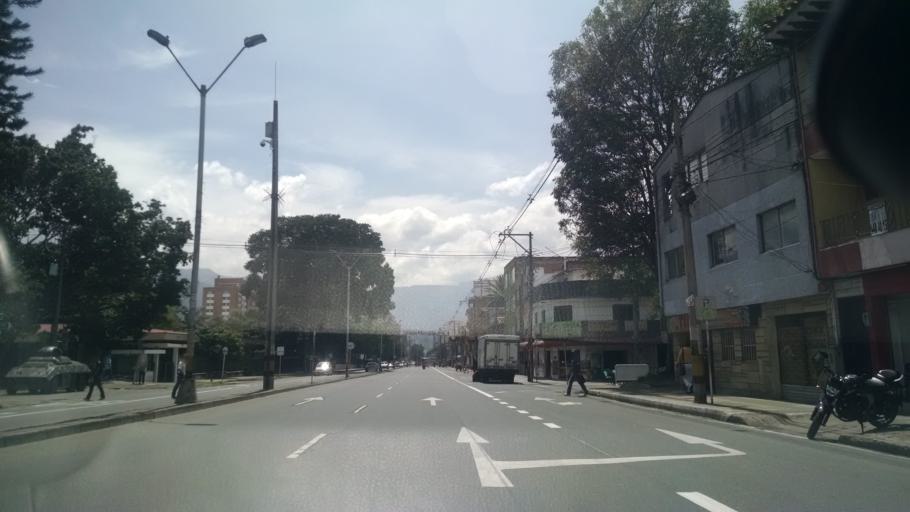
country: CO
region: Antioquia
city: Medellin
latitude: 6.2620
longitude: -75.5936
